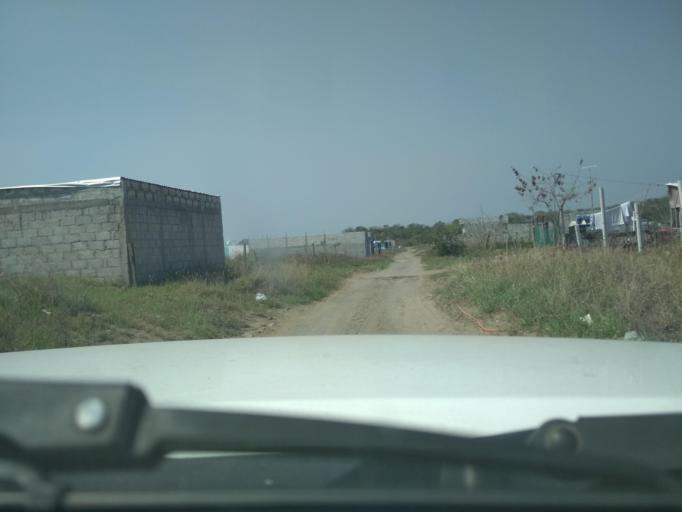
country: MX
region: Veracruz
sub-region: Veracruz
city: Lomas de Rio Medio Cuatro
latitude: 19.1952
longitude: -96.1975
